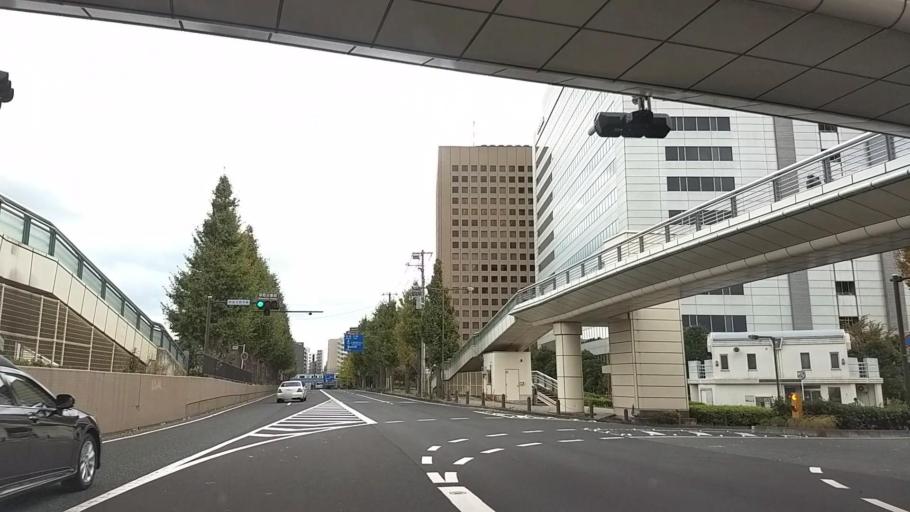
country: JP
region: Kanagawa
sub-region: Kawasaki-shi
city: Kawasaki
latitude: 35.5375
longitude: 139.6995
